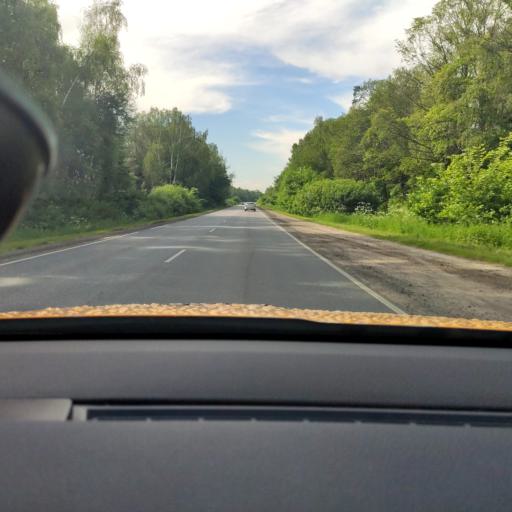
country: RU
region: Moskovskaya
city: Zhilevo
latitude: 54.9493
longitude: 38.0089
